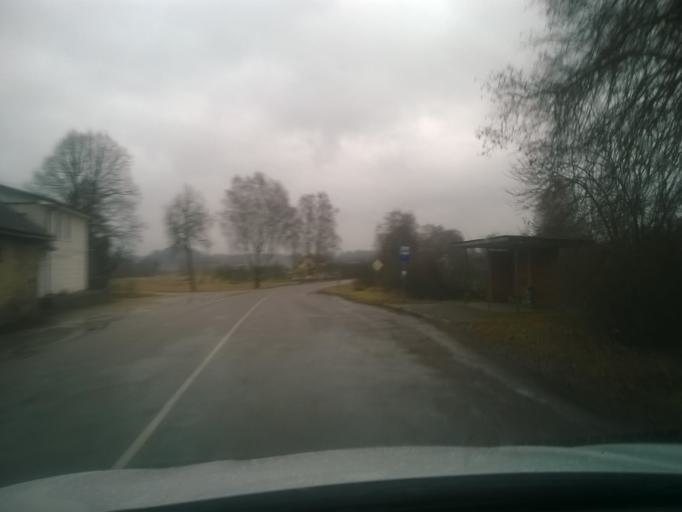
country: LV
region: Jaunpils
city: Jaunpils
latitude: 56.9095
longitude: 22.9673
